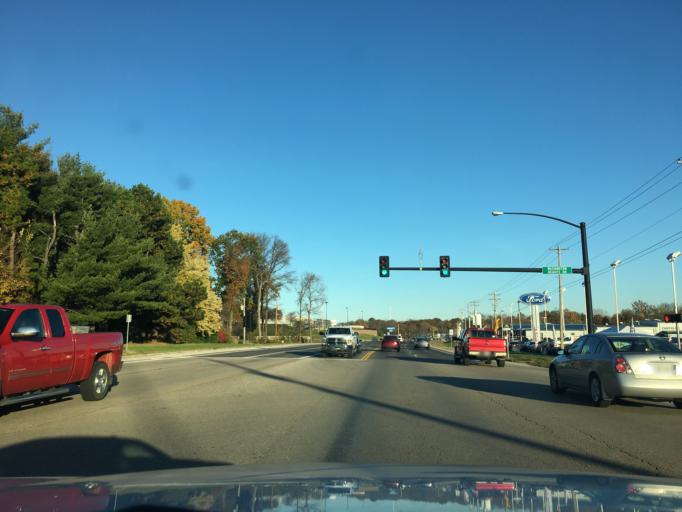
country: US
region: Missouri
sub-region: Franklin County
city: Washington
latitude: 38.5389
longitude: -90.9990
